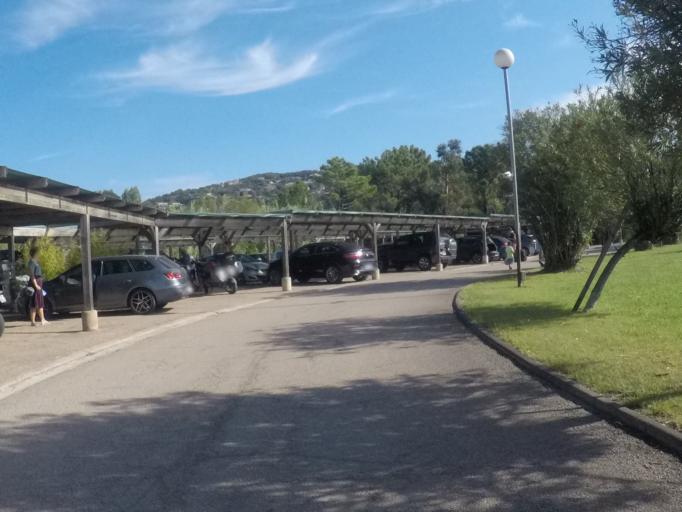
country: FR
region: Corsica
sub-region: Departement de la Corse-du-Sud
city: Porto-Vecchio
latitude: 41.6106
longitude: 9.2854
